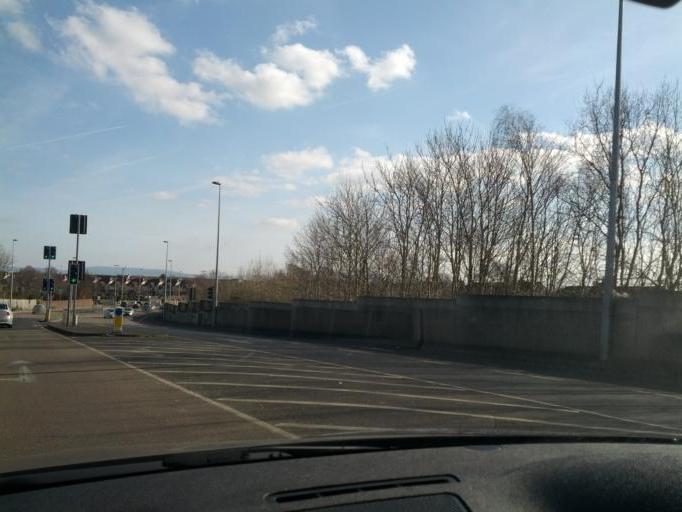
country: IE
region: Leinster
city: Lucan
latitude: 53.3565
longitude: -6.4231
